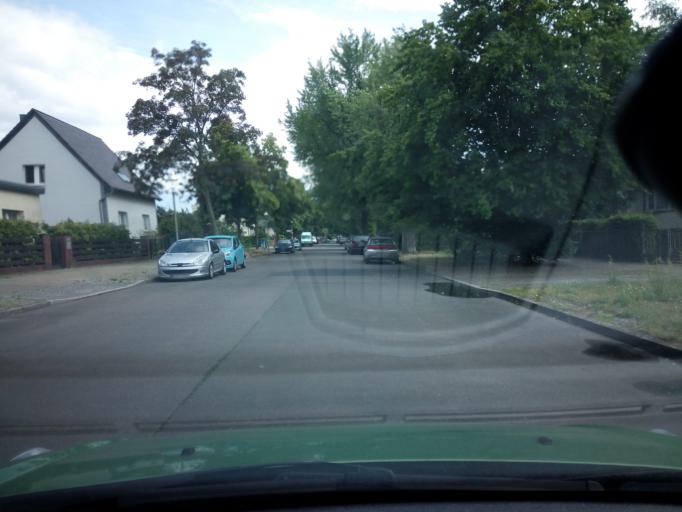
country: DE
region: Berlin
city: Rudow
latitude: 52.4278
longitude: 13.4948
